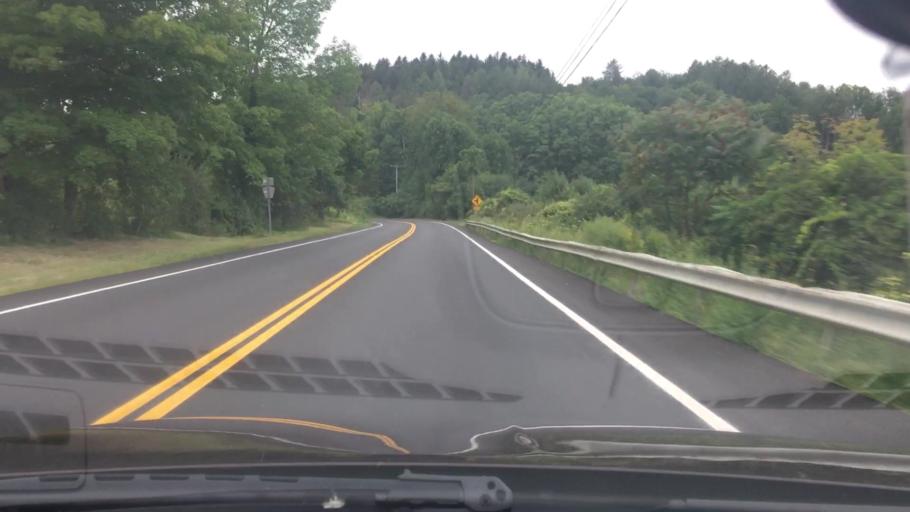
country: US
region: New York
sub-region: Dutchess County
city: Dover Plains
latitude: 41.8465
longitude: -73.5835
